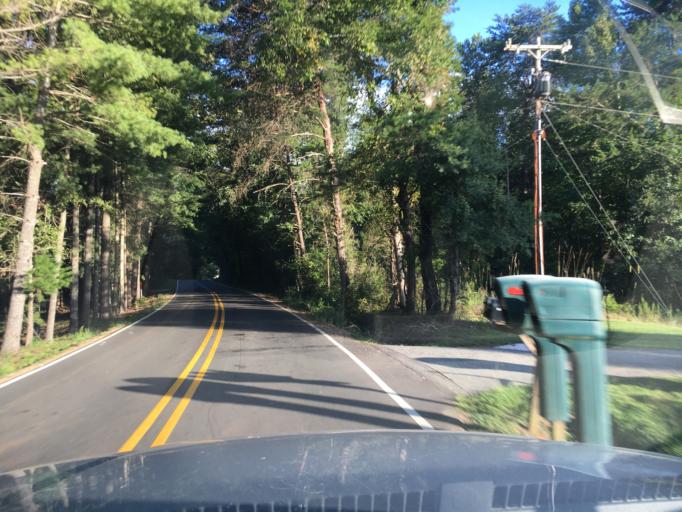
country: US
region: South Carolina
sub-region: Spartanburg County
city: Roebuck
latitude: 34.8931
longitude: -82.0285
